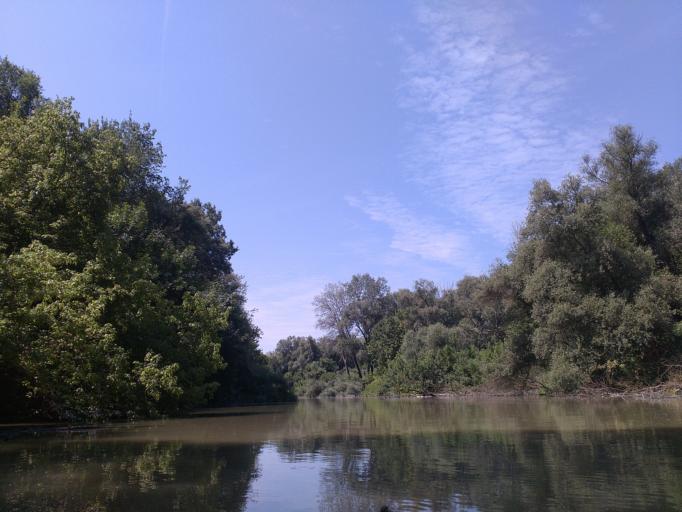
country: SK
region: Nitriansky
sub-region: Okres Nove Zamky
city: Sturovo
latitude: 47.7634
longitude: 18.6885
